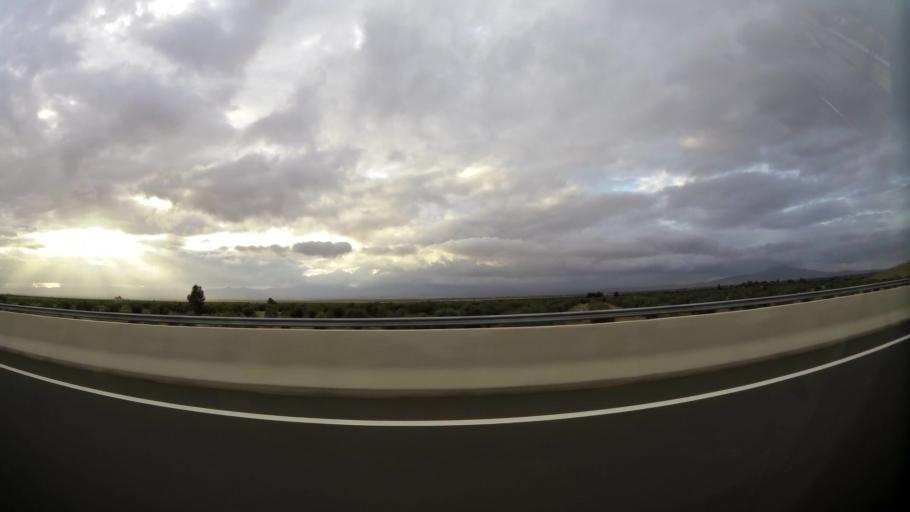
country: MA
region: Taza-Al Hoceima-Taounate
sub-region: Taza
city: Guercif
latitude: 34.3258
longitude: -3.3499
